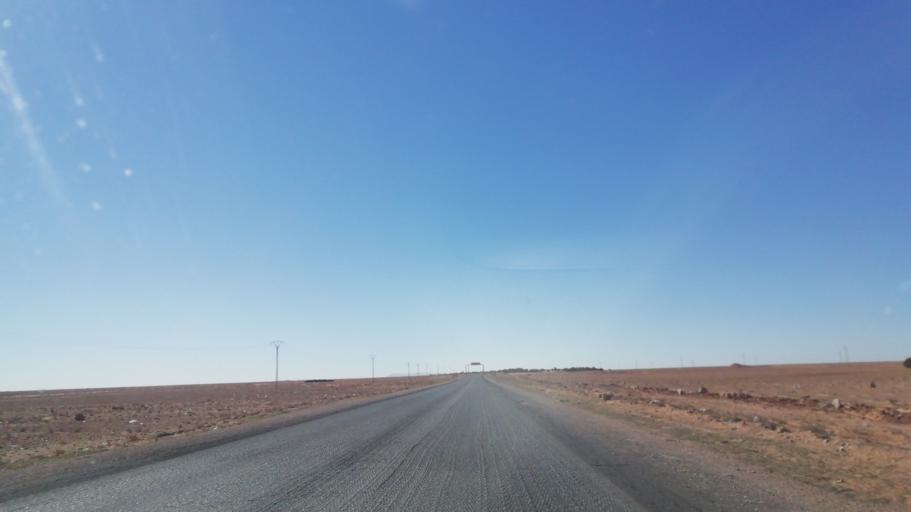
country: DZ
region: Saida
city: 'Ain el Hadjar
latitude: 34.0102
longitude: 0.0529
